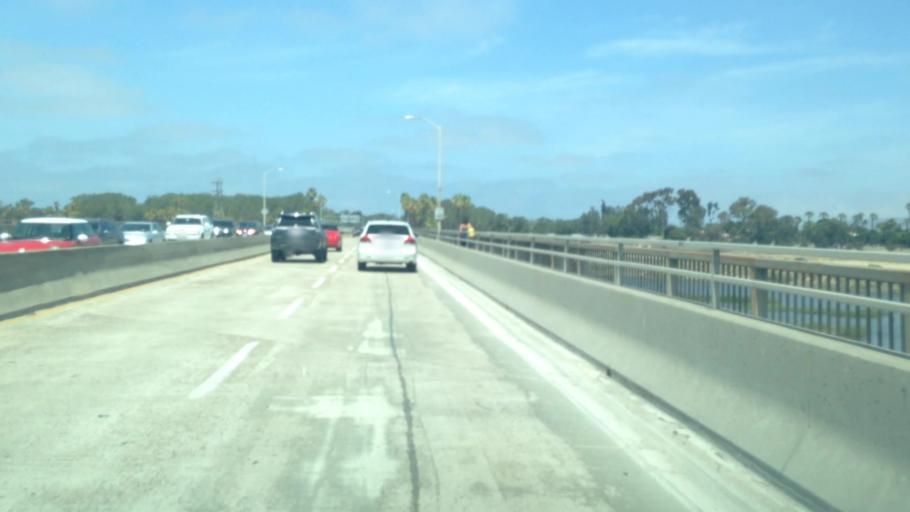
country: US
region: California
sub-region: San Diego County
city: San Diego
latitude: 32.7583
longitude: -117.2250
